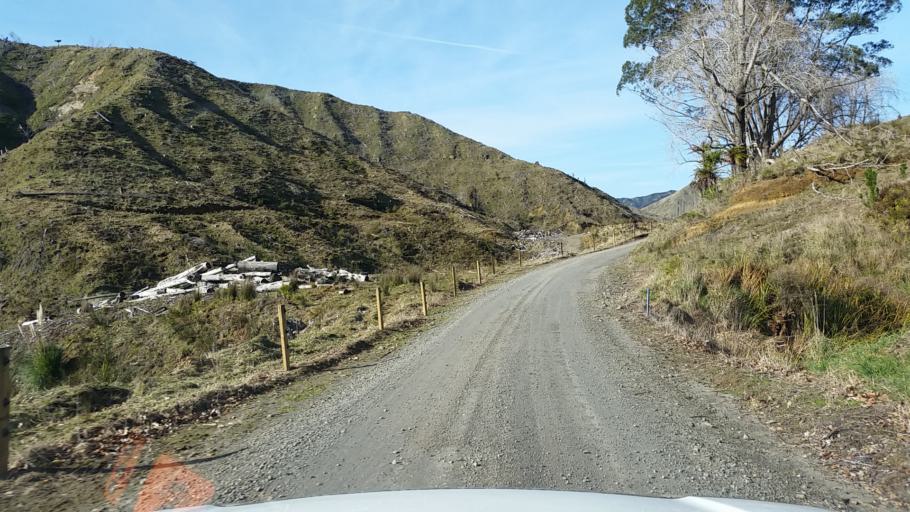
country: NZ
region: Taranaki
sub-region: South Taranaki District
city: Eltham
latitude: -39.3612
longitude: 174.5143
